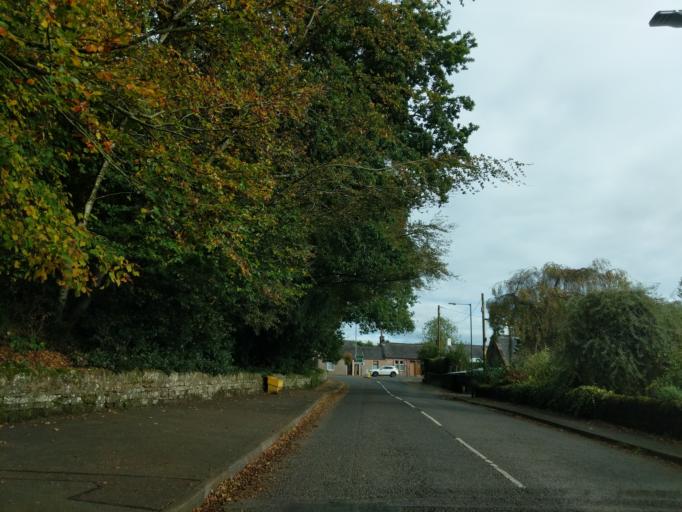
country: GB
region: Scotland
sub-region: Dumfries and Galloway
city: Thornhill
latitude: 55.2435
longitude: -3.7700
